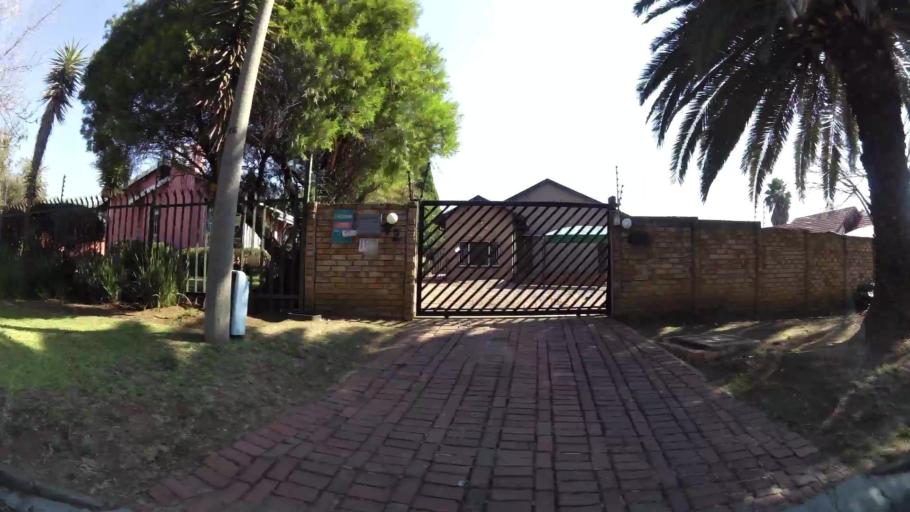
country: ZA
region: Gauteng
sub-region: City of Johannesburg Metropolitan Municipality
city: Modderfontein
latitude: -26.1131
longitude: 28.1658
